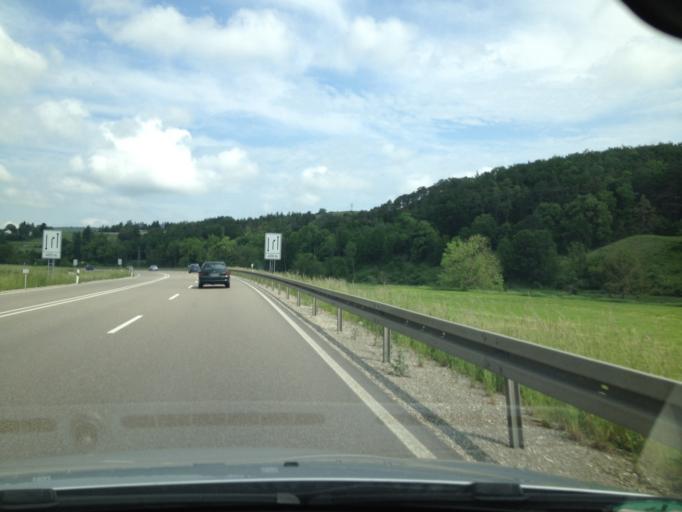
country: DE
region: Bavaria
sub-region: Swabia
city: Harburg
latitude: 48.7760
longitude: 10.7019
